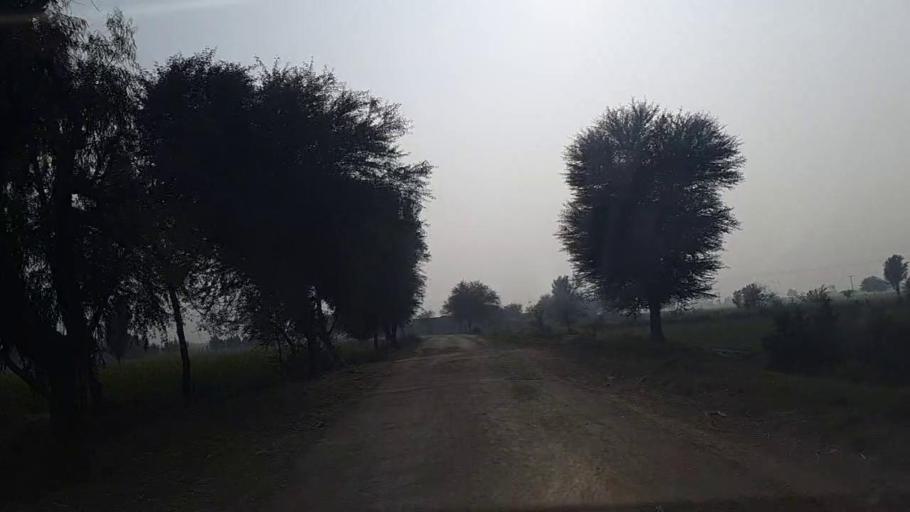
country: PK
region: Sindh
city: Sanghar
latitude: 26.0866
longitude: 68.8771
